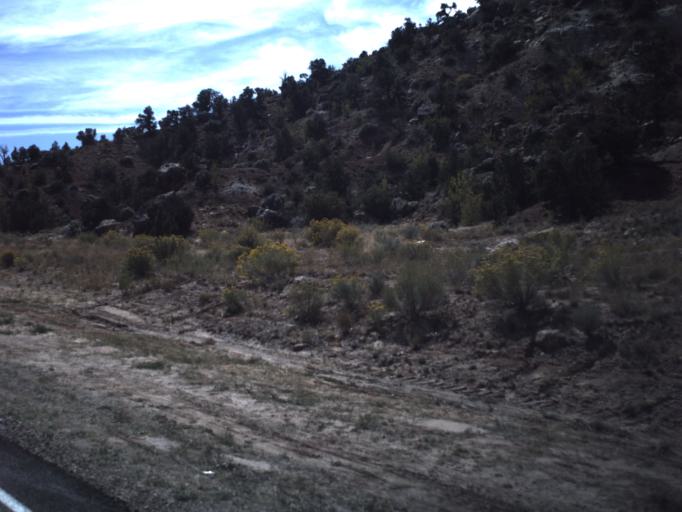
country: US
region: Utah
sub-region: Wayne County
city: Loa
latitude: 37.7754
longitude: -111.6182
